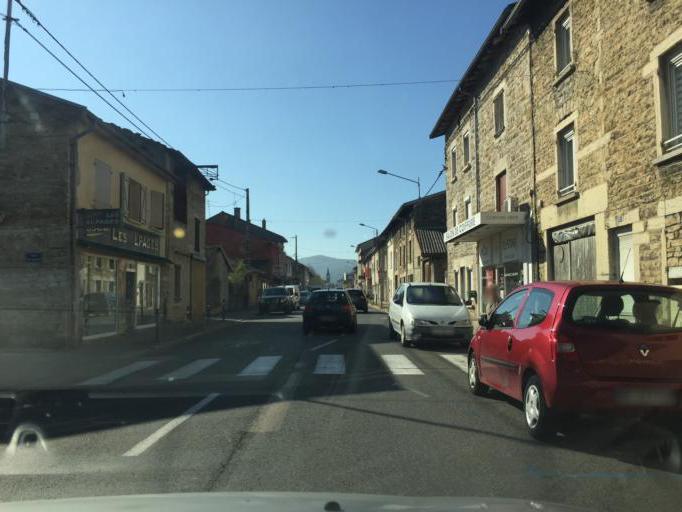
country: FR
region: Rhone-Alpes
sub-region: Departement de l'Ain
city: Amberieu-en-Bugey
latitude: 45.9661
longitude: 5.3550
